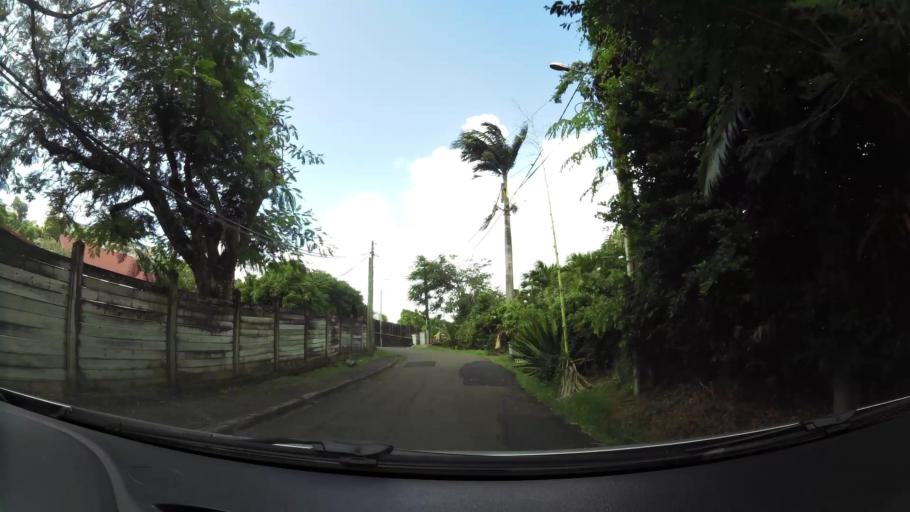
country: MQ
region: Martinique
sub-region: Martinique
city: Fort-de-France
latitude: 14.6333
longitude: -61.0511
